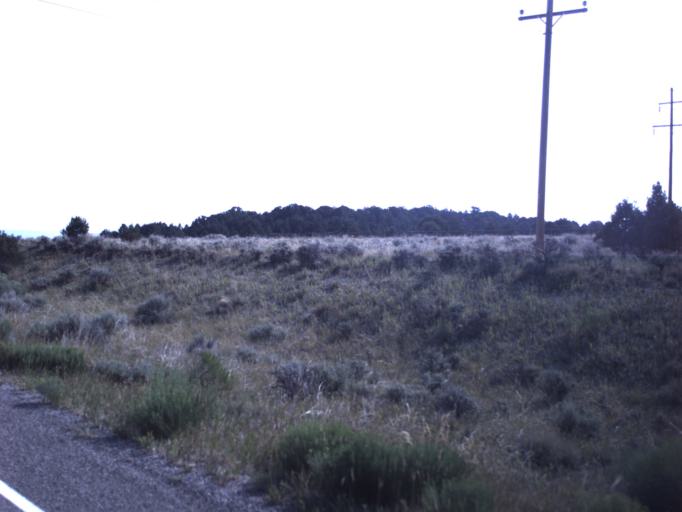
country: US
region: Utah
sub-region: Daggett County
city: Manila
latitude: 40.9590
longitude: -109.4699
